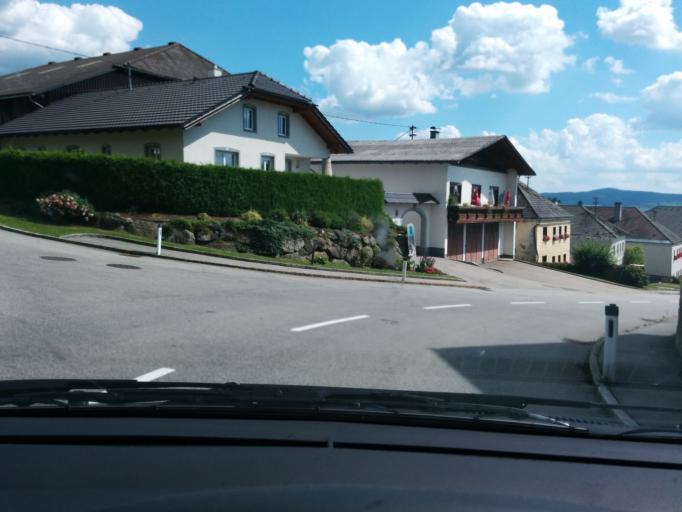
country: AT
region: Upper Austria
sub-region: Politischer Bezirk Rohrbach
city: Ulrichsberg
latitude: 48.7076
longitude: 13.9022
